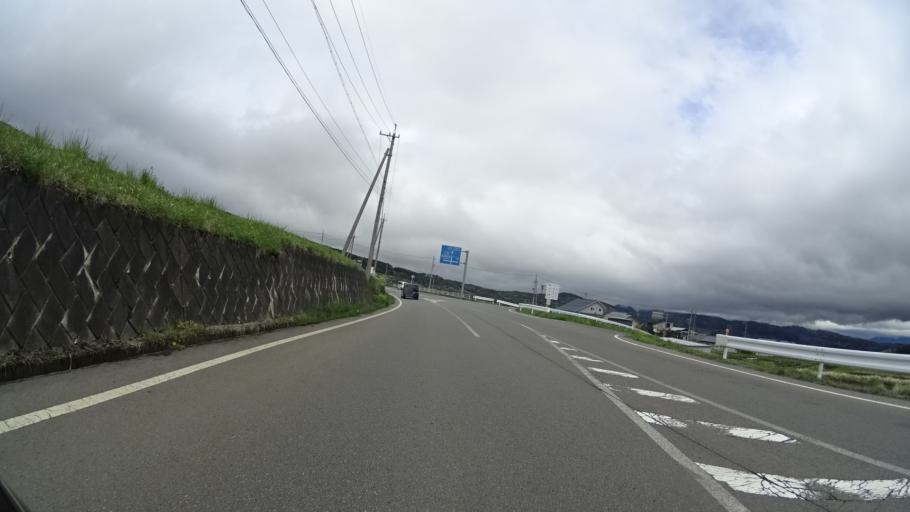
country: JP
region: Nagano
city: Nagano-shi
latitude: 36.7317
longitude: 138.2086
